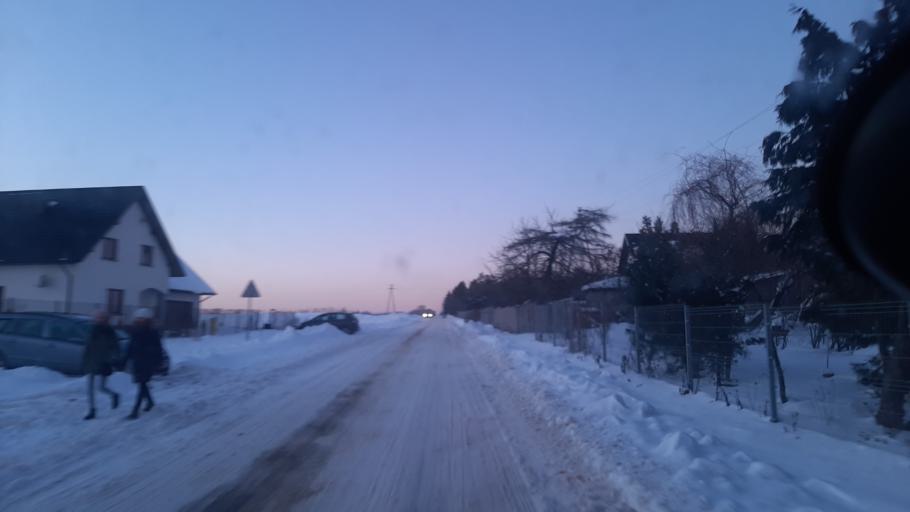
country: PL
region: Lublin Voivodeship
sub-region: Powiat lubelski
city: Jastkow
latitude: 51.3639
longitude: 22.5285
